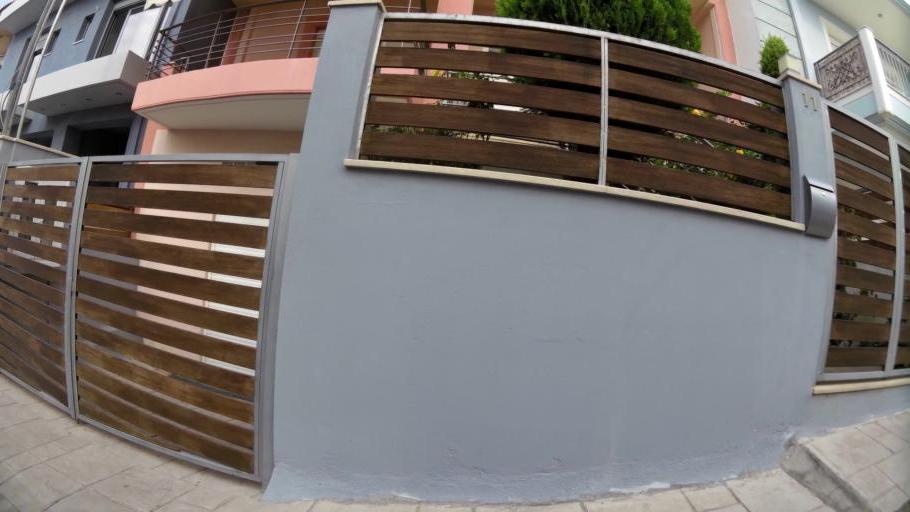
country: GR
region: Attica
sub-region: Nomarchia Athinas
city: Kamateron
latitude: 38.0579
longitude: 23.7043
